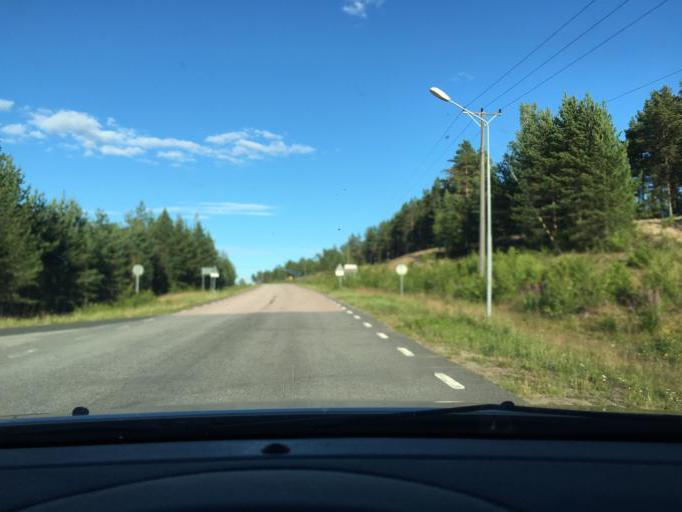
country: SE
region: Norrbotten
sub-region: Haparanda Kommun
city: Haparanda
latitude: 65.7337
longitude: 23.7529
